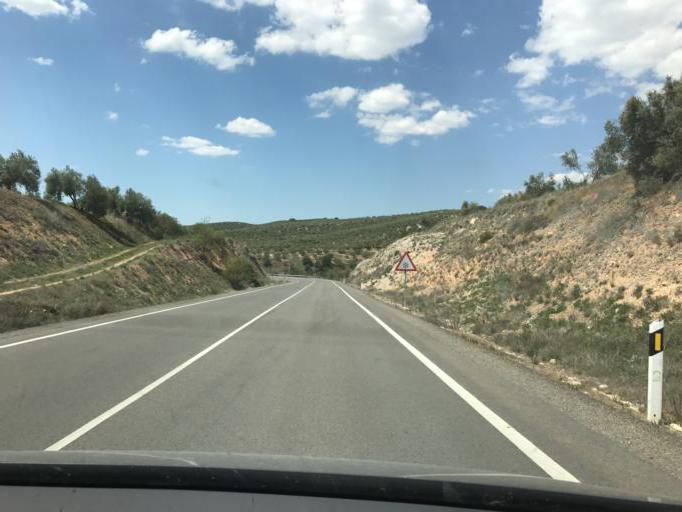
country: ES
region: Andalusia
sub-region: Provincia de Jaen
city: Frailes
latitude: 37.4361
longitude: -3.8082
